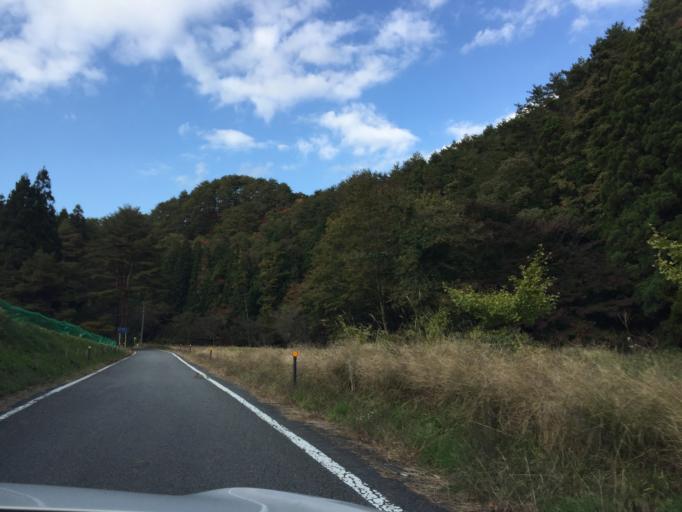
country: JP
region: Fukushima
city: Iwaki
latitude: 37.2235
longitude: 140.7592
